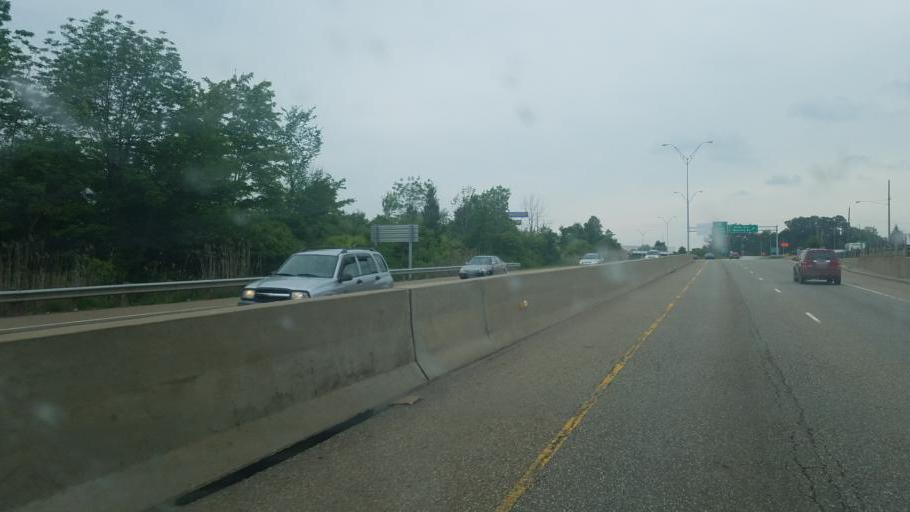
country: US
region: Ohio
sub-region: Summit County
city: Sawyerwood
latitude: 41.0253
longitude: -81.4781
